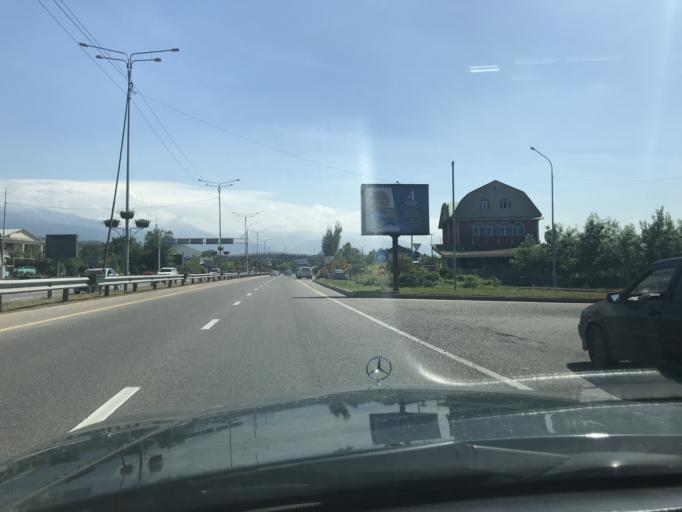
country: KZ
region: Almaty Qalasy
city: Almaty
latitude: 43.2815
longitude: 76.9860
